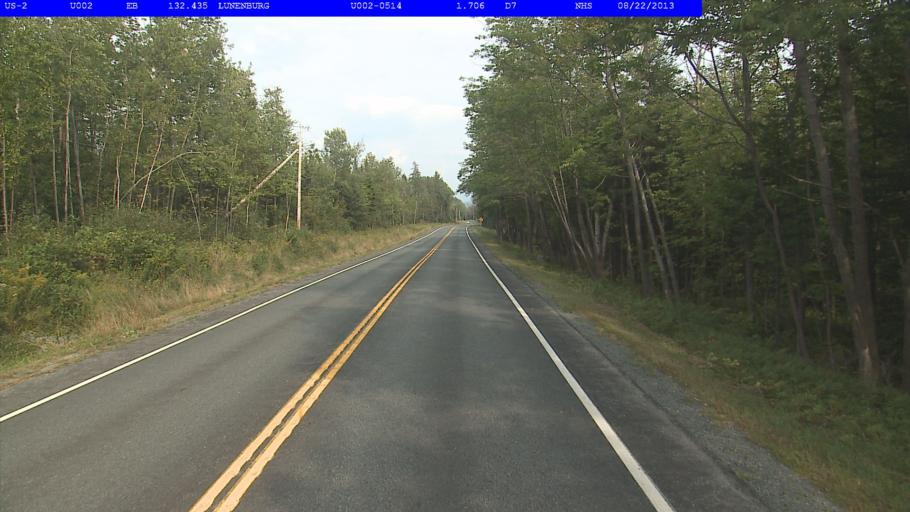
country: US
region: New Hampshire
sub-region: Coos County
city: Whitefield
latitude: 44.4647
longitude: -71.7417
